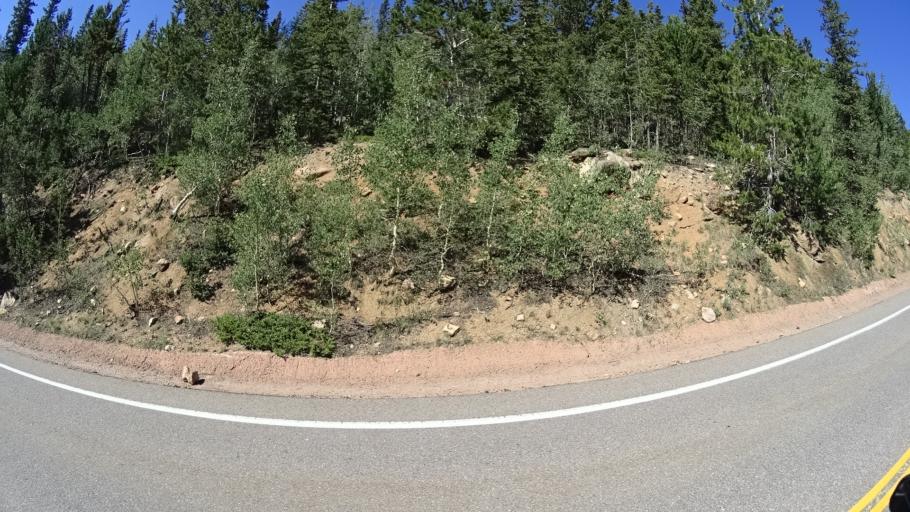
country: US
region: Colorado
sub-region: El Paso County
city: Cascade-Chipita Park
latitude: 38.8931
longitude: -105.0670
